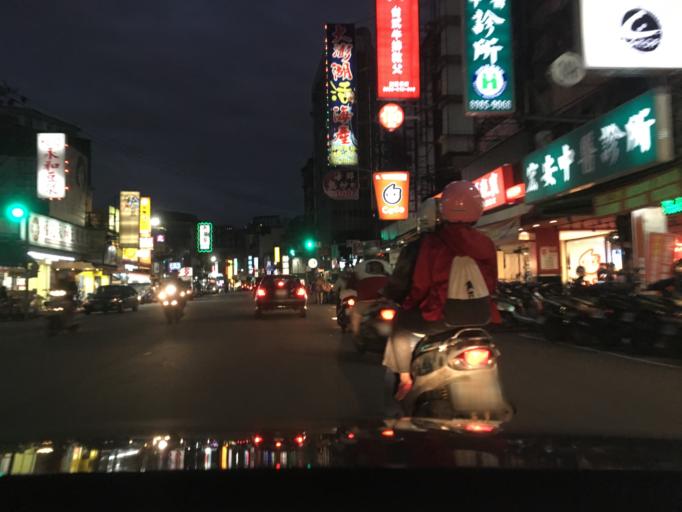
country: TW
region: Taipei
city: Taipei
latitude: 25.0676
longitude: 121.4926
